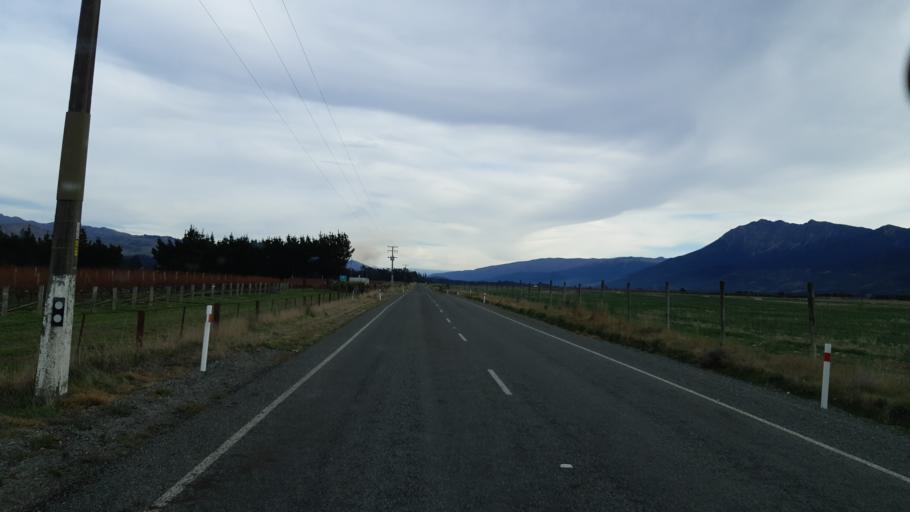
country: NZ
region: Tasman
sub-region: Tasman District
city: Richmond
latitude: -41.6134
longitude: 173.3877
